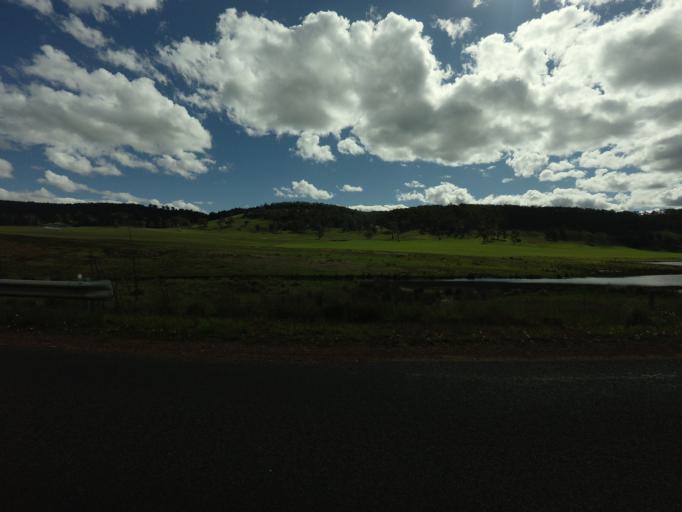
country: AU
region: Tasmania
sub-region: Brighton
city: Bridgewater
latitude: -42.4232
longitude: 147.3119
